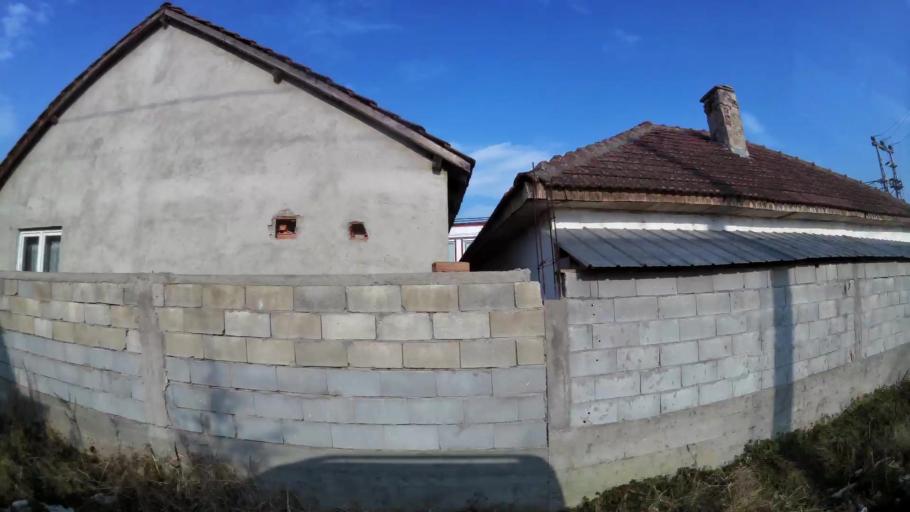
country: MK
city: Creshevo
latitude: 42.0212
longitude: 21.5018
